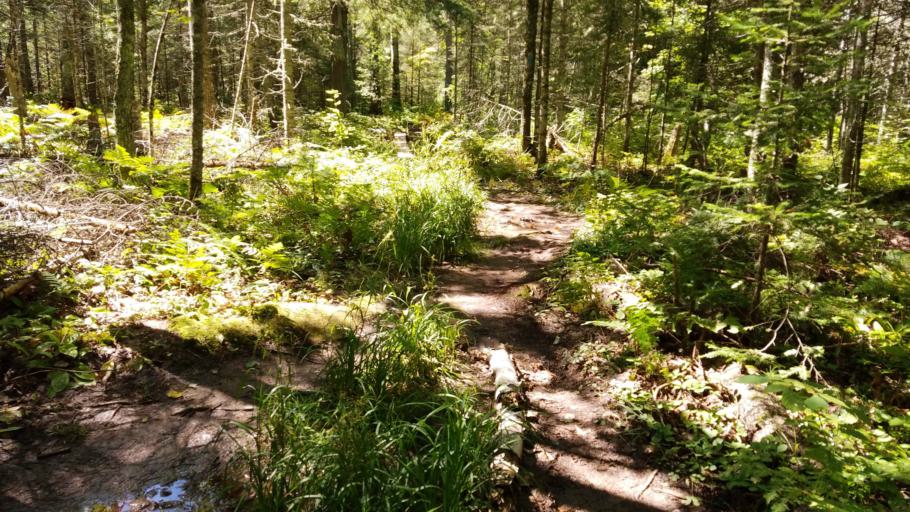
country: US
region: Michigan
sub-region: Ontonagon County
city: Ontonagon
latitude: 46.6499
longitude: -89.1702
